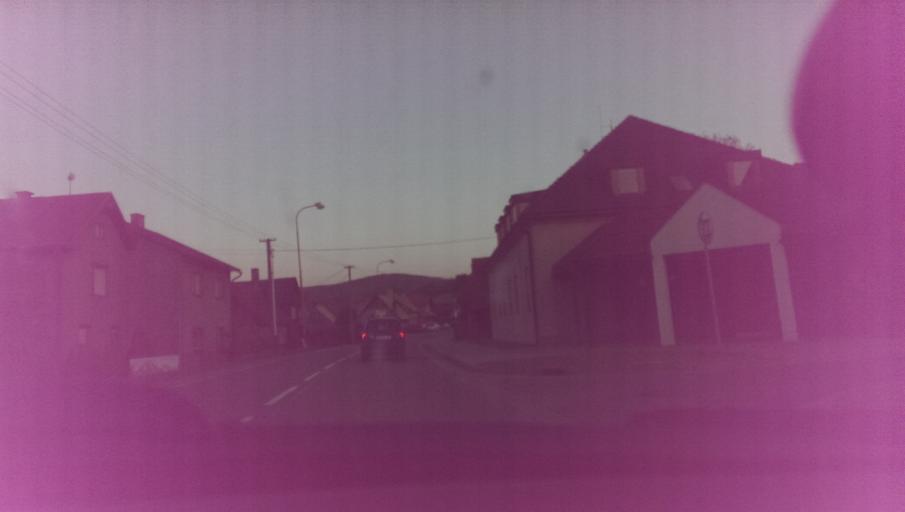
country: CZ
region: Zlin
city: Valasska Polanka
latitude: 49.2624
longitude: 17.9967
